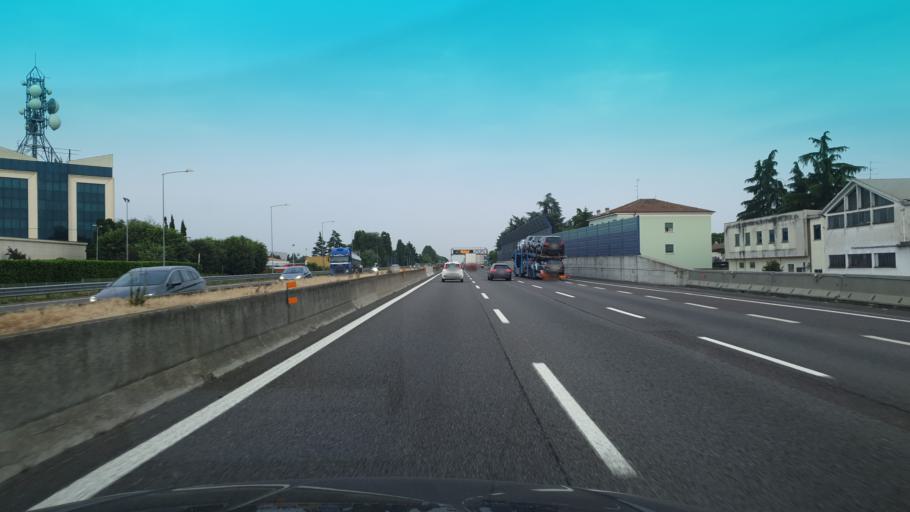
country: IT
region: Lombardy
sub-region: Provincia di Brescia
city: Roncadelle
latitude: 45.5310
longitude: 10.1529
